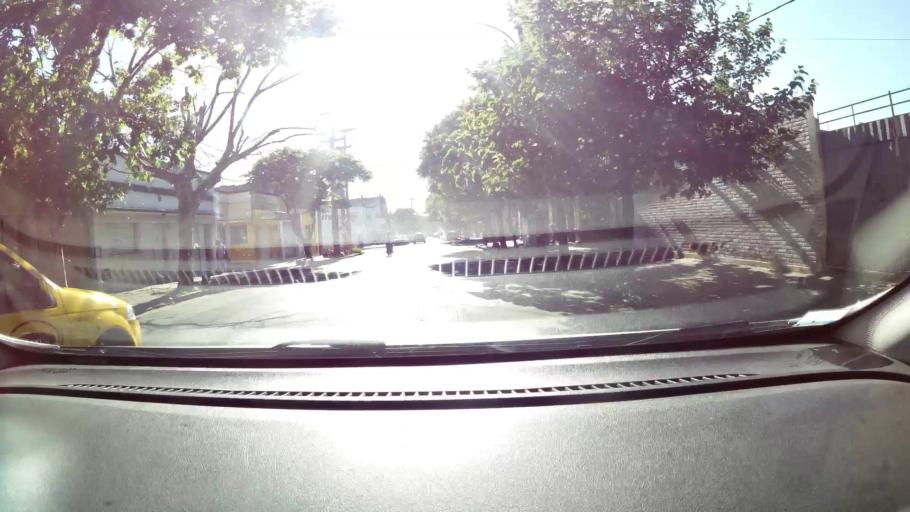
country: AR
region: Cordoba
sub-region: Departamento de Capital
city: Cordoba
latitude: -31.4245
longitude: -64.1601
